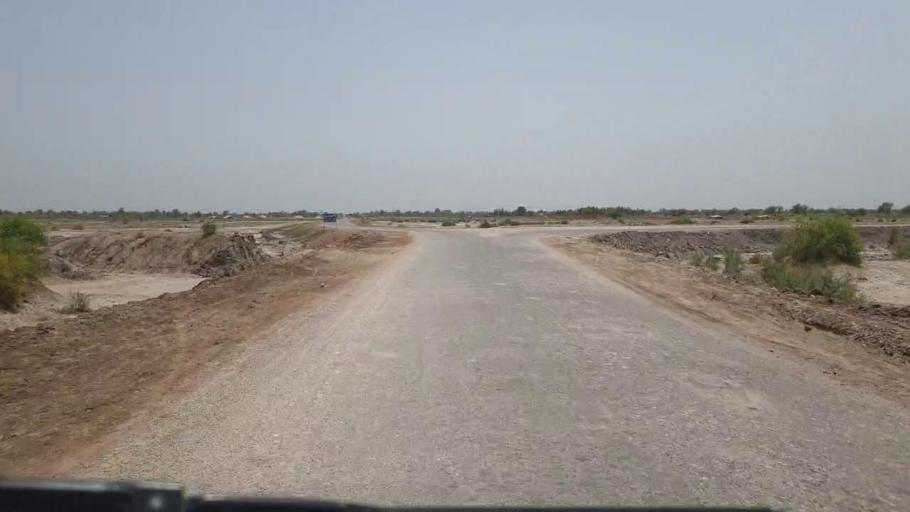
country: PK
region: Sindh
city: Daulatpur
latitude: 26.4565
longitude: 68.1184
